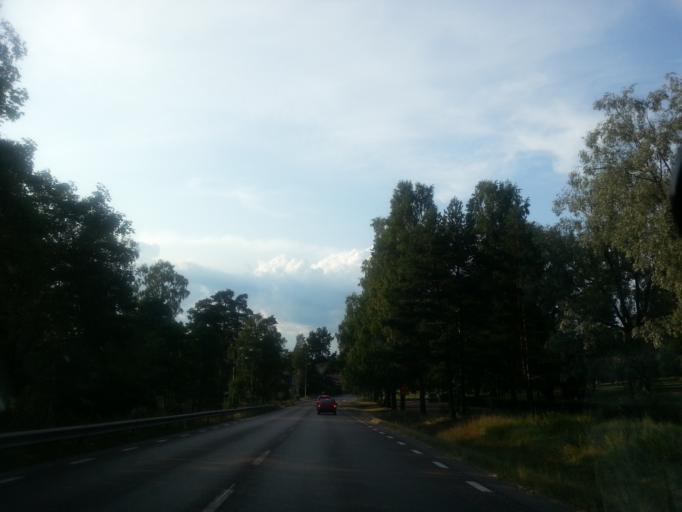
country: SE
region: Dalarna
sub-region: Avesta Kommun
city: Horndal
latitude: 60.2879
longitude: 16.4027
